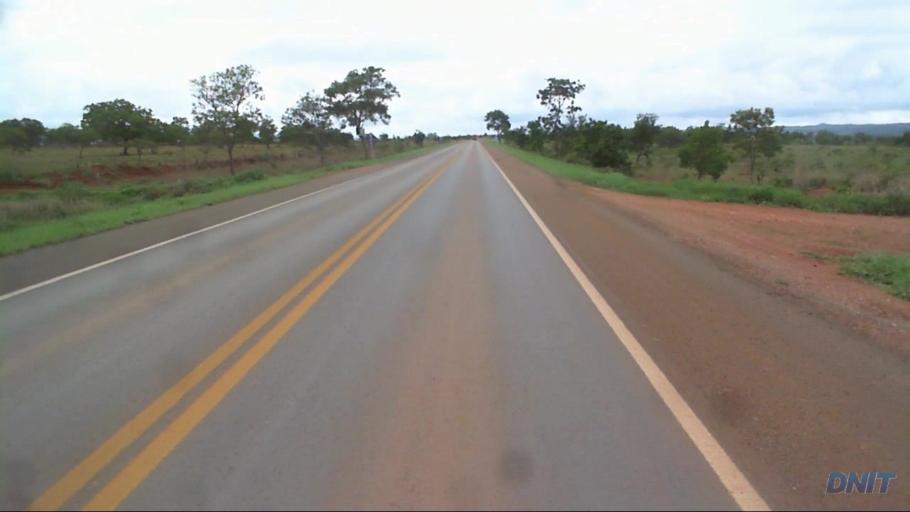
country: BR
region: Goias
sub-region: Padre Bernardo
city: Padre Bernardo
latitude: -15.1501
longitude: -48.3435
